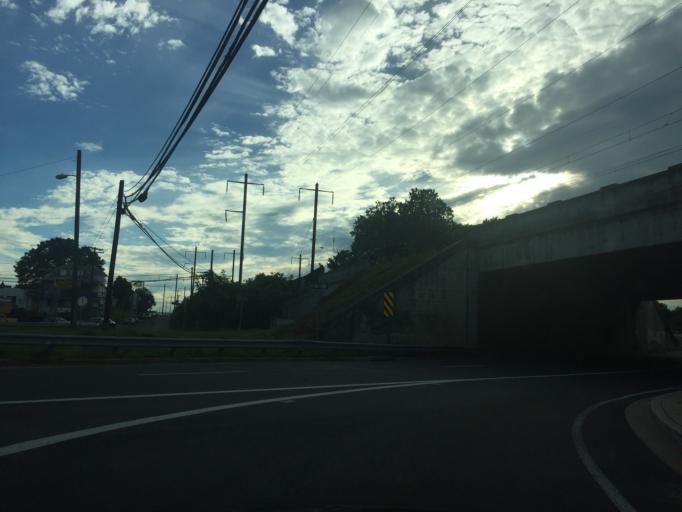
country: US
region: Maryland
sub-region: Baltimore County
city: Middle River
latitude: 39.3325
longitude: -76.4384
